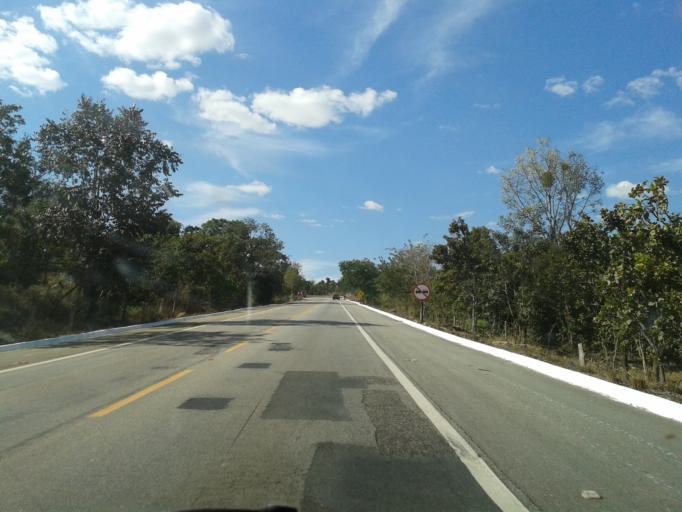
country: BR
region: Goias
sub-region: Goias
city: Goias
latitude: -15.8701
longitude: -50.0907
